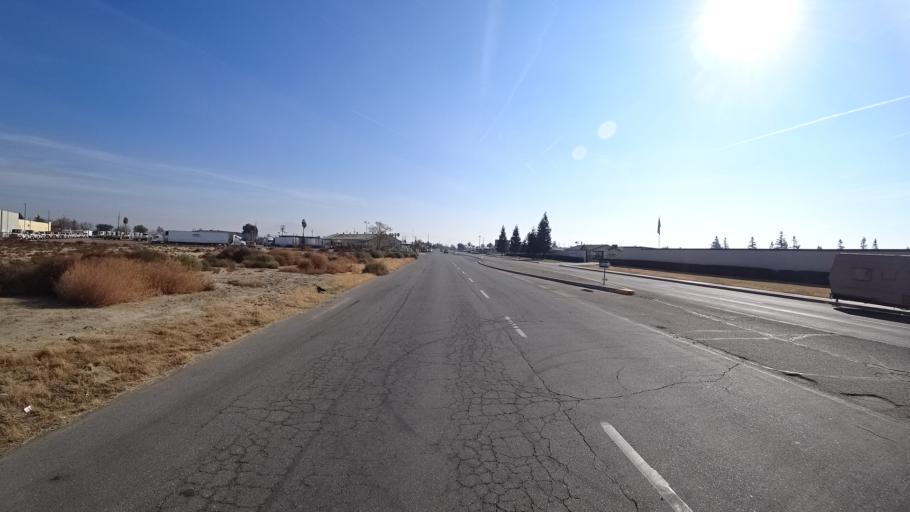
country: US
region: California
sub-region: Kern County
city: Greenfield
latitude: 35.3211
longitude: -119.0064
